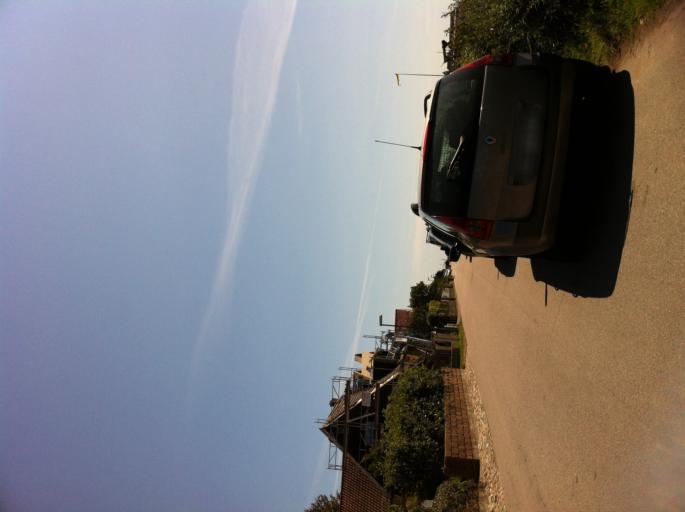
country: SE
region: Skane
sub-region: Hoganas Kommun
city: Hoganas
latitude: 56.1788
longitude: 12.5560
